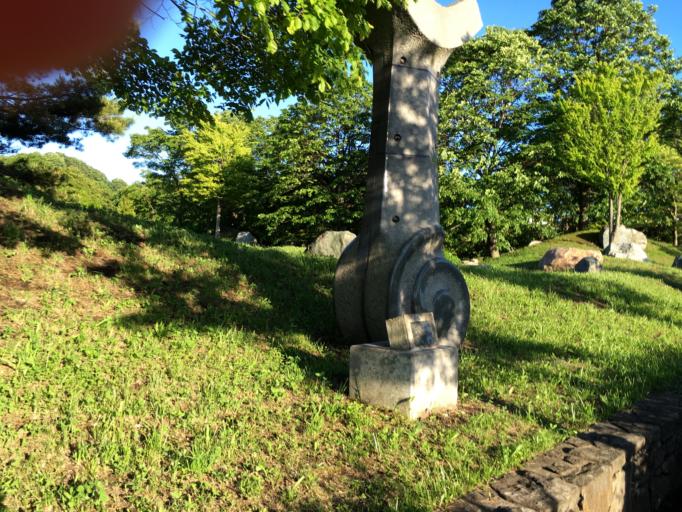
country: JP
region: Hokkaido
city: Muroran
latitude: 42.3207
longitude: 140.9760
